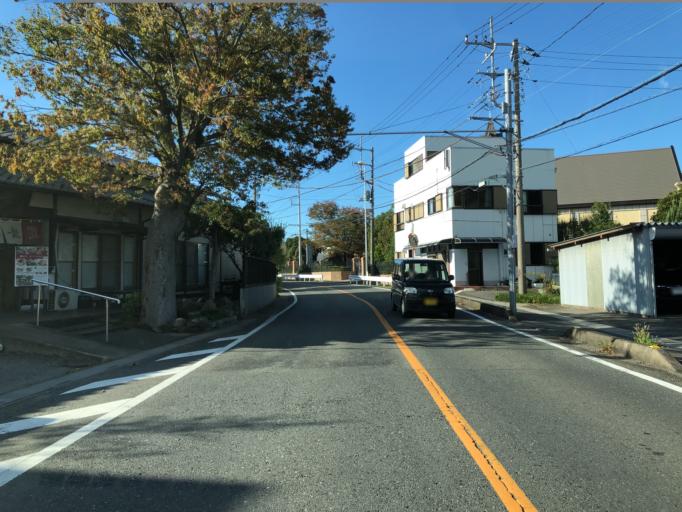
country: JP
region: Saitama
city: Fukiage-fujimi
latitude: 36.0380
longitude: 139.4184
